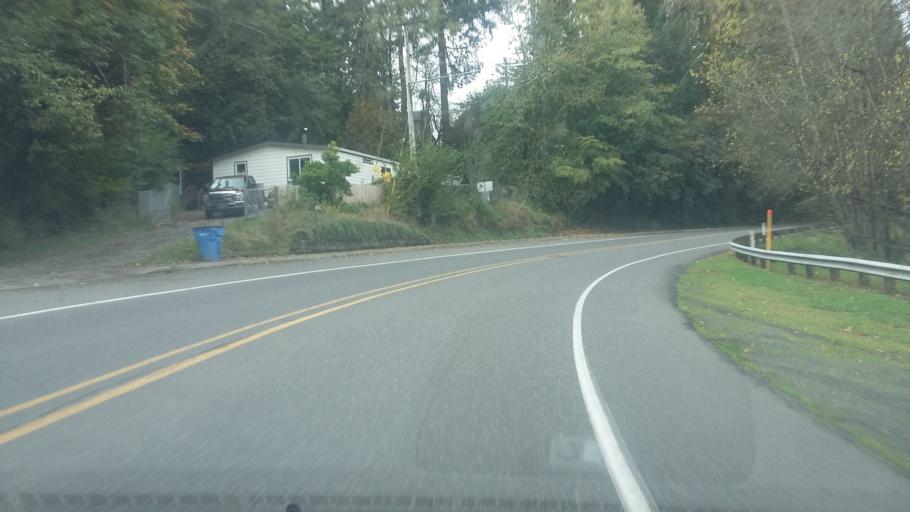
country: US
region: Washington
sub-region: Clark County
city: Ridgefield
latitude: 45.8152
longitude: -122.7330
